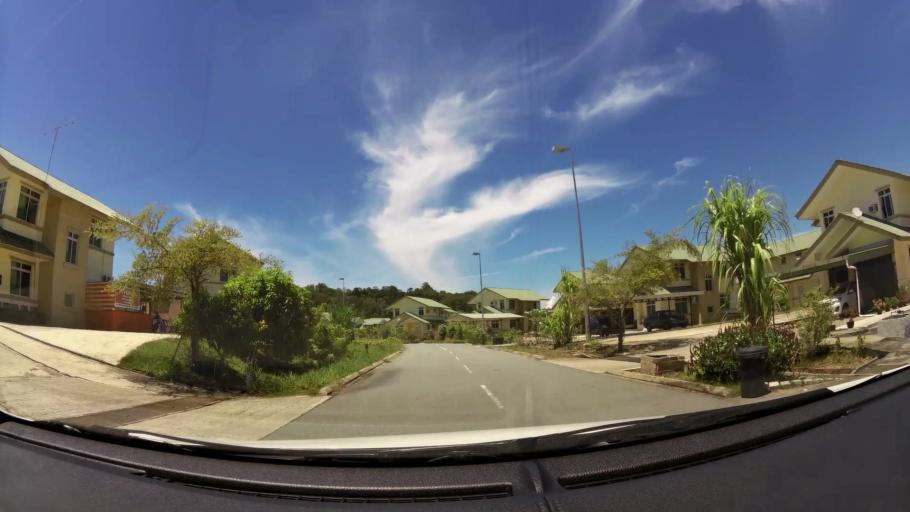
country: BN
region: Brunei and Muara
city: Bandar Seri Begawan
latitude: 5.0270
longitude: 115.0327
